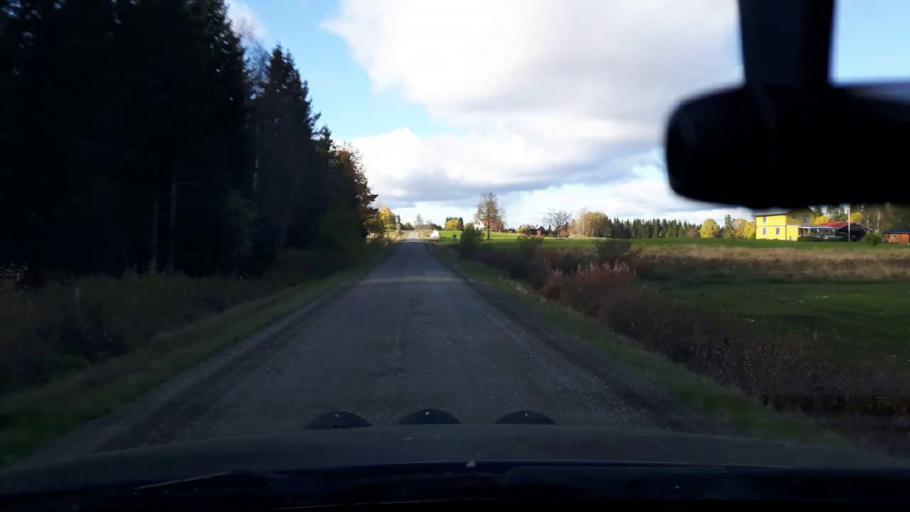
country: SE
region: Jaemtland
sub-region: Bergs Kommun
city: Hoverberg
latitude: 63.0225
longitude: 14.2994
